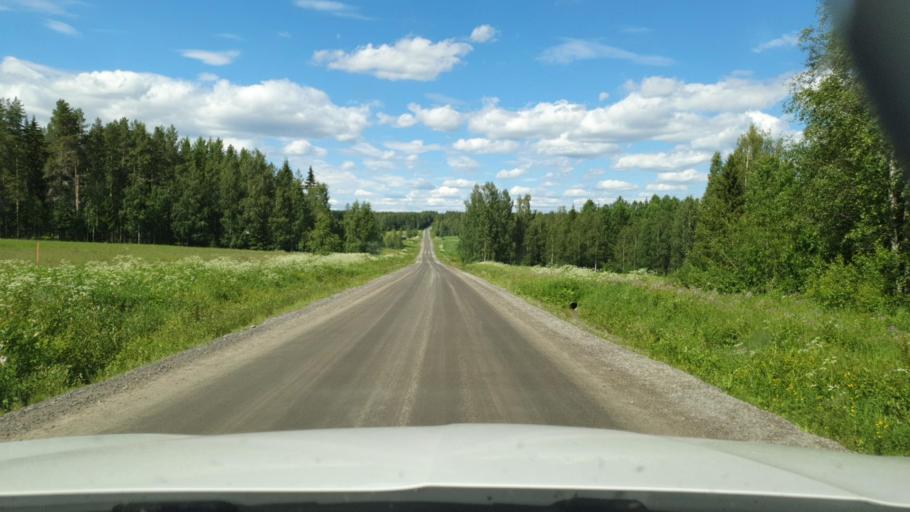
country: SE
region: Vaesterbotten
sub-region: Skelleftea Kommun
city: Forsbacka
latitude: 64.7852
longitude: 20.5128
